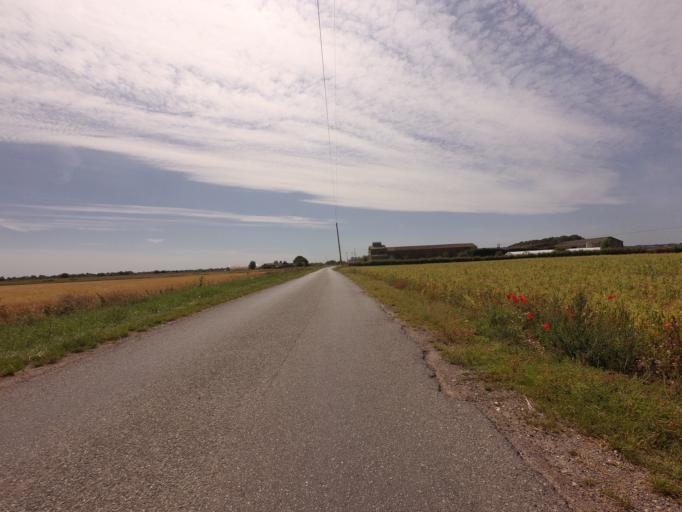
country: GB
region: England
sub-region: Kent
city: Stone
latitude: 51.0169
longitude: 0.7938
